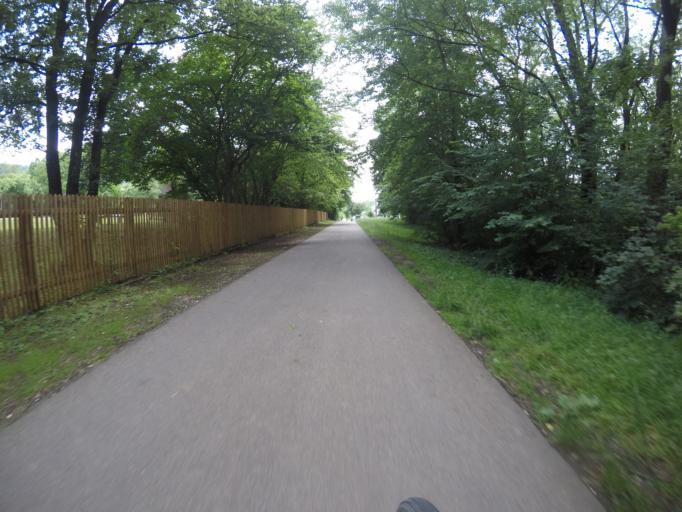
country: DE
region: Baden-Wuerttemberg
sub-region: Regierungsbezirk Stuttgart
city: Kuchen
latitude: 48.6455
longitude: 9.7974
